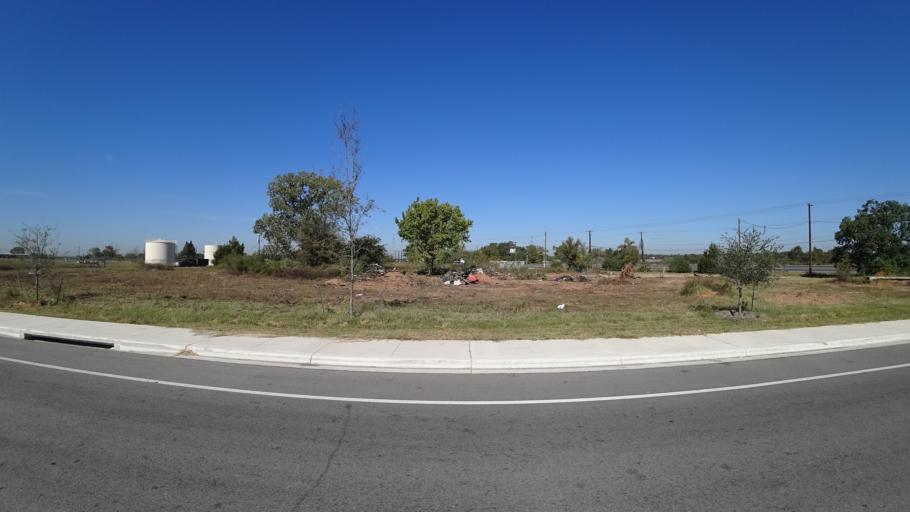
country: US
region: Texas
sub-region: Travis County
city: Hornsby Bend
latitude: 30.2506
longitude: -97.5962
